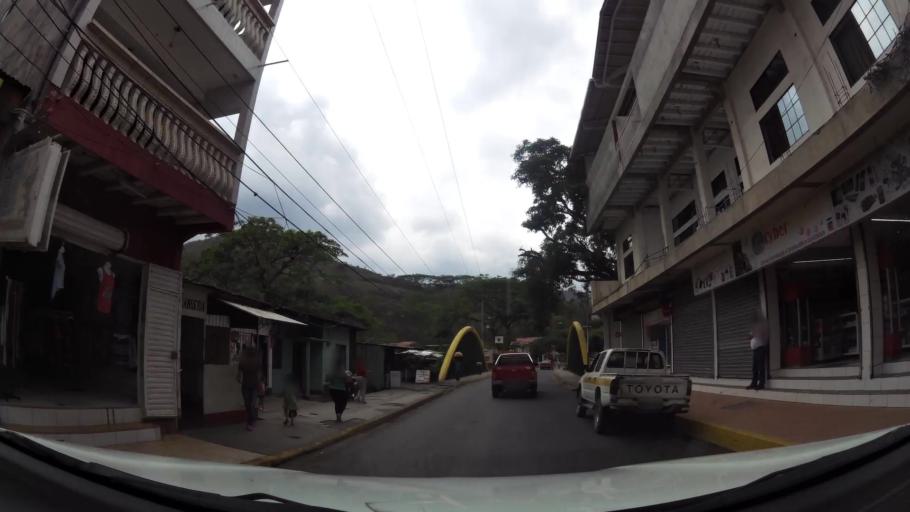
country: NI
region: Matagalpa
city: Matagalpa
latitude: 12.9315
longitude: -85.9194
